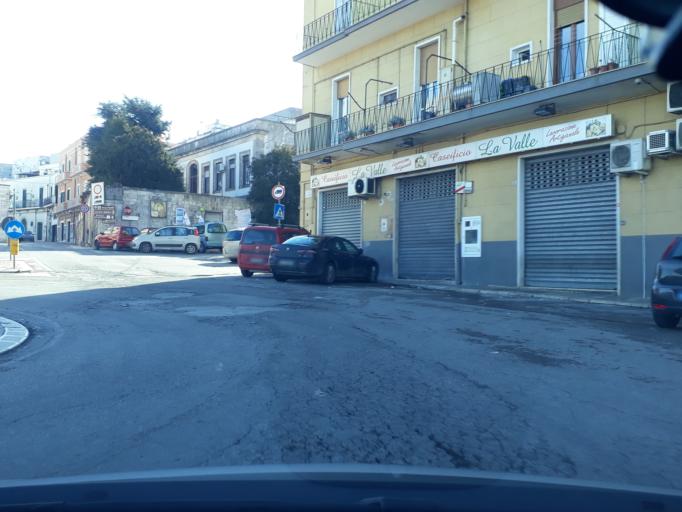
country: IT
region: Apulia
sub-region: Provincia di Taranto
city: Martina Franca
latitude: 40.7070
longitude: 17.3388
